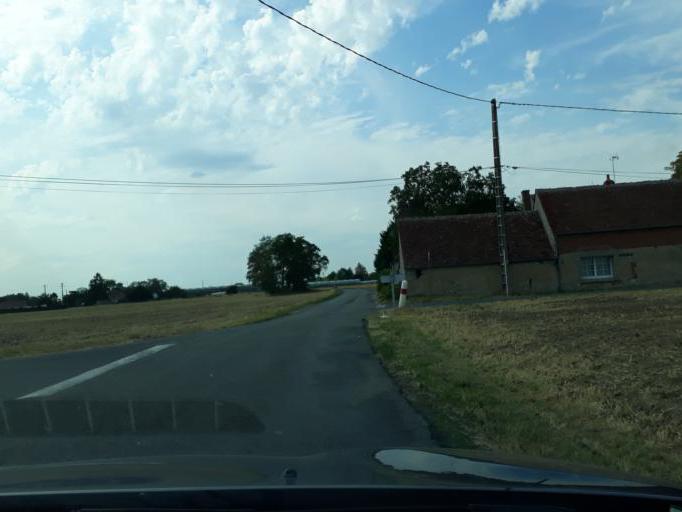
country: FR
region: Centre
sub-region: Departement du Loiret
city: Jargeau
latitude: 47.8446
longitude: 2.1707
